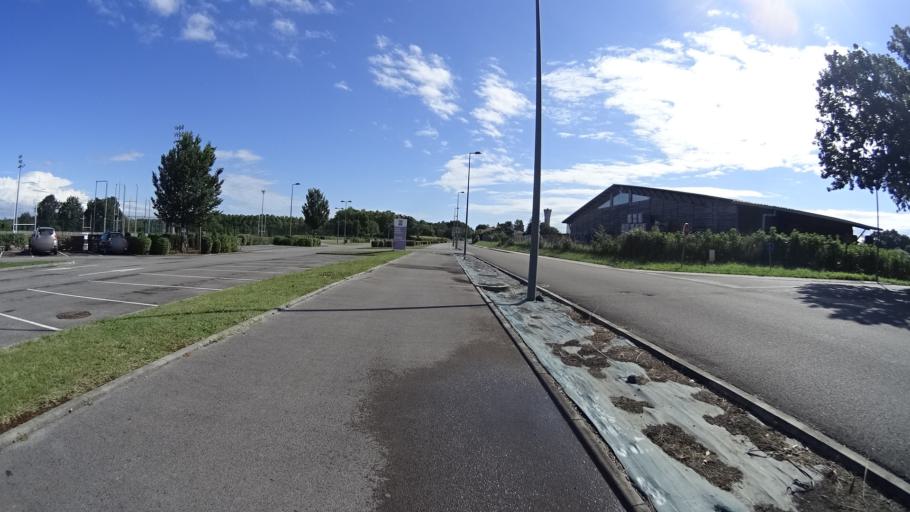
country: FR
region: Aquitaine
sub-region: Departement des Landes
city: Oeyreluy
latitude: 43.6939
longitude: -1.0809
